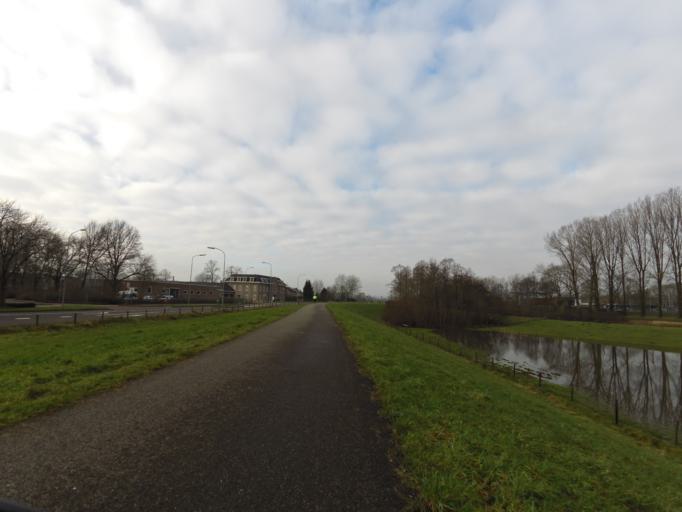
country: NL
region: Gelderland
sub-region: Gemeente Doesburg
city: Doesburg
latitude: 52.0057
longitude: 6.1327
